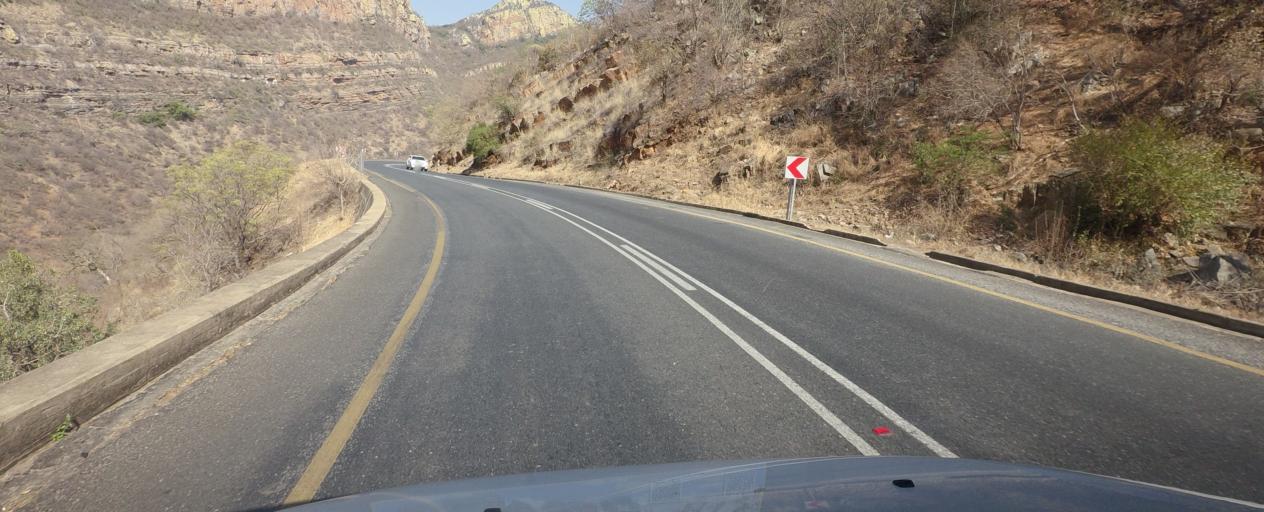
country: ZA
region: Limpopo
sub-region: Mopani District Municipality
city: Hoedspruit
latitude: -24.4522
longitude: 30.6107
